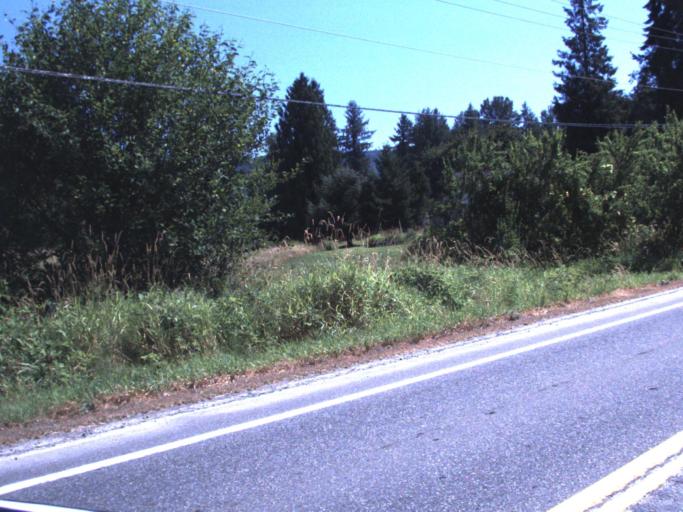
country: US
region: Washington
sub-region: King County
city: Fall City
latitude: 47.5745
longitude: -121.9165
